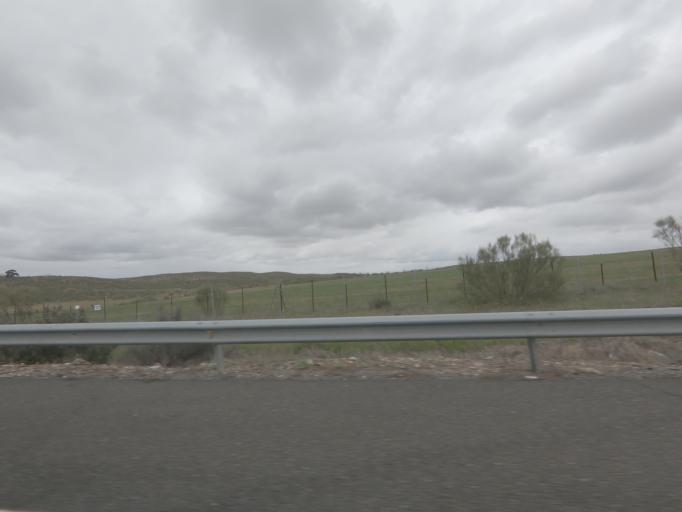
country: ES
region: Extremadura
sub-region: Provincia de Caceres
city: Galisteo
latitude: 39.9383
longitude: -6.2074
